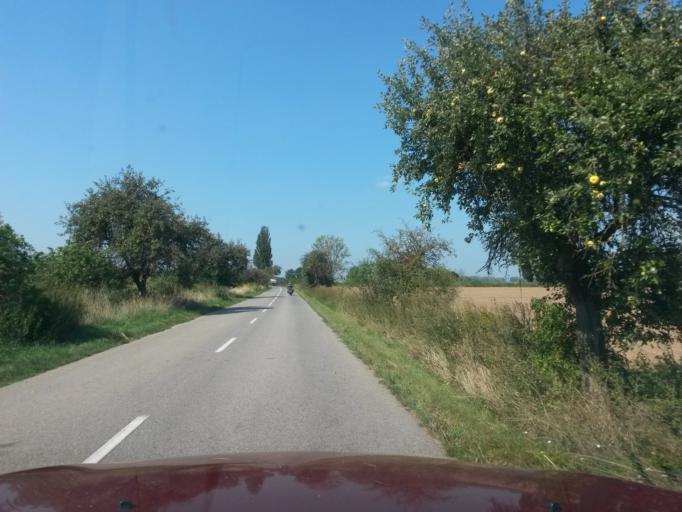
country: HU
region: Borsod-Abauj-Zemplen
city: Gonc
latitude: 48.5325
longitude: 21.1490
